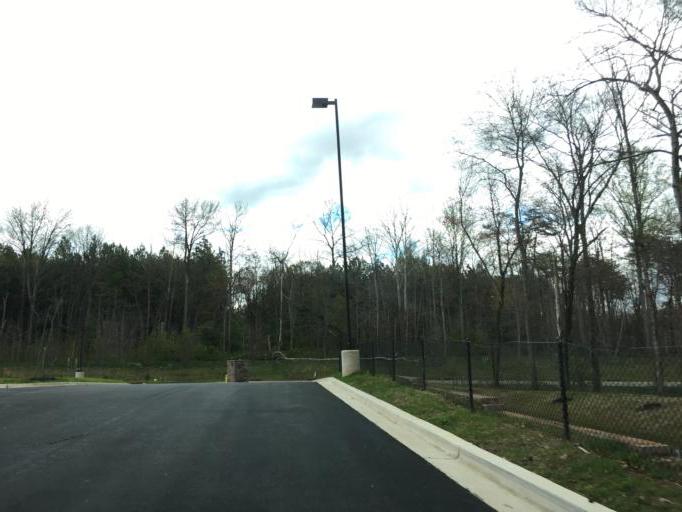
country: US
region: Maryland
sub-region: Howard County
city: Hanover
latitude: 39.1784
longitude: -76.7160
